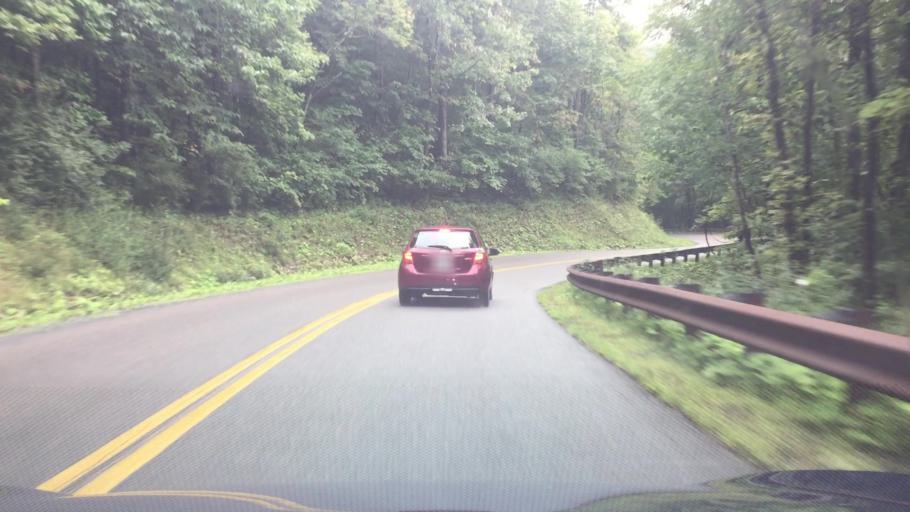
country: US
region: Virginia
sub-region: Smyth County
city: Atkins
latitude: 36.8138
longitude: -81.4069
